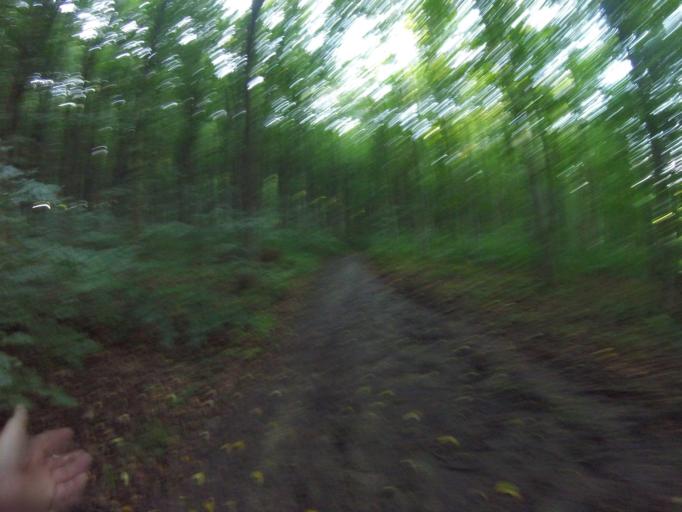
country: HU
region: Zala
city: Letenye
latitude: 46.5106
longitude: 16.7140
